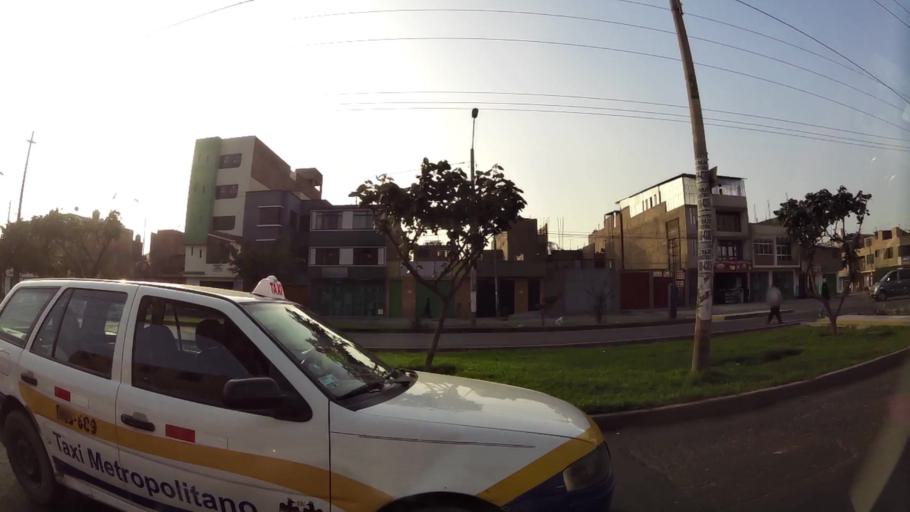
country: PE
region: Lima
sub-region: Lima
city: Independencia
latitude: -11.9468
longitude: -77.0743
